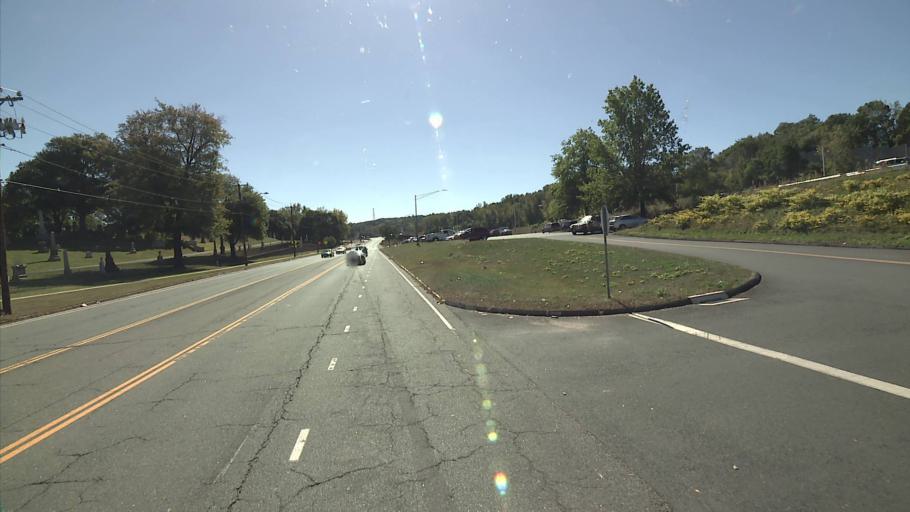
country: US
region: Connecticut
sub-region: New Haven County
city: Waterbury
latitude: 41.5451
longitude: -73.0256
